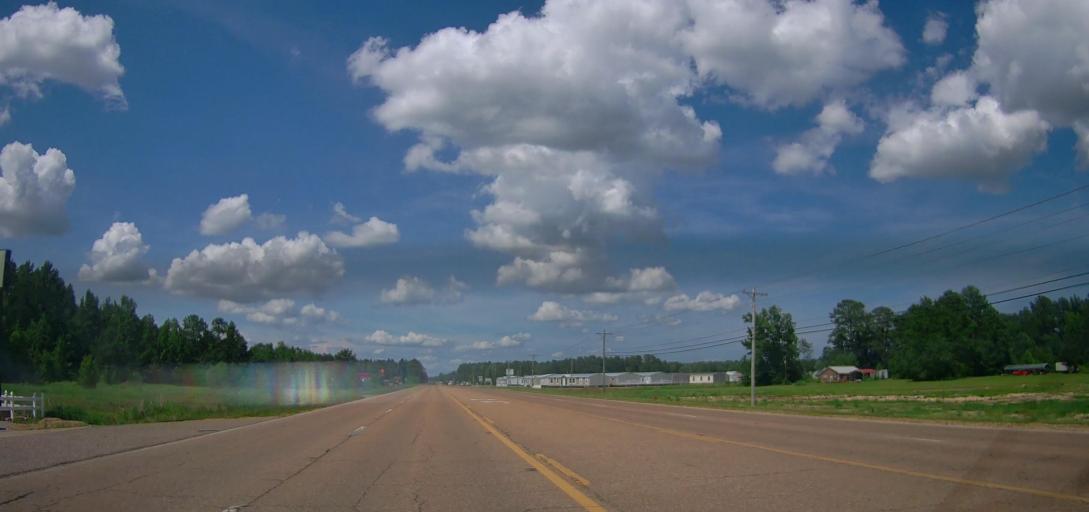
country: US
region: Mississippi
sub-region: Lowndes County
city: Columbus Air Force Base
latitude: 33.5928
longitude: -88.4255
